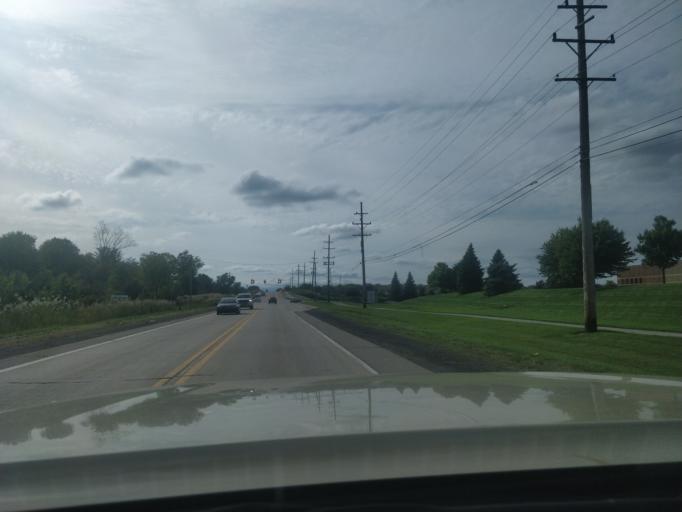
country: US
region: Michigan
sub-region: Wayne County
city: Woodhaven
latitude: 42.1550
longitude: -83.2378
